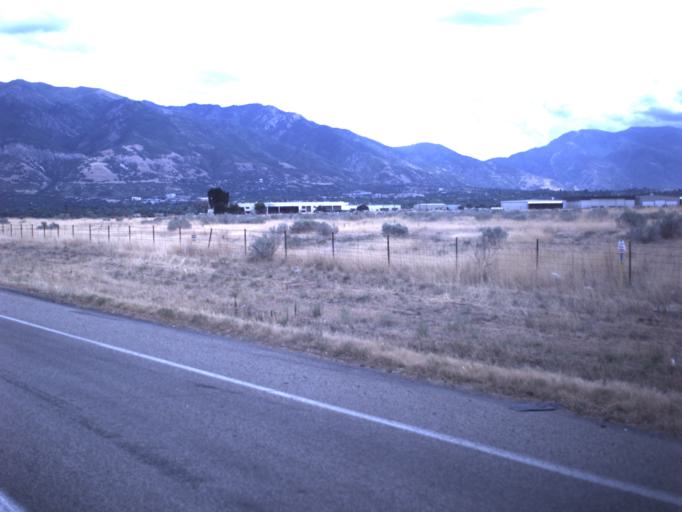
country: US
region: Utah
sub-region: Weber County
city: Riverdale
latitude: 41.2048
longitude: -112.0061
